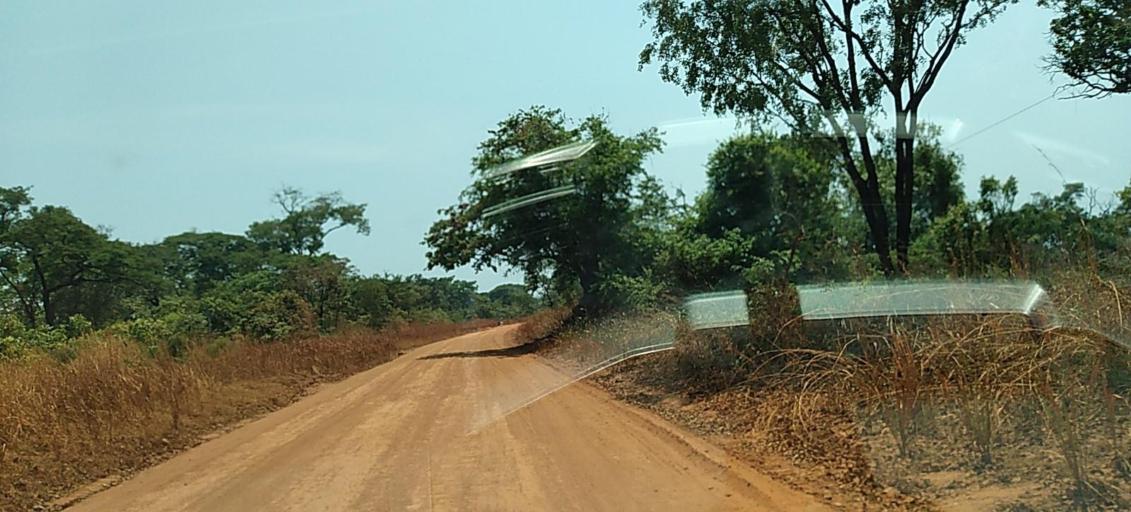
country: CD
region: Katanga
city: Kipushi
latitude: -11.9731
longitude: 26.8954
